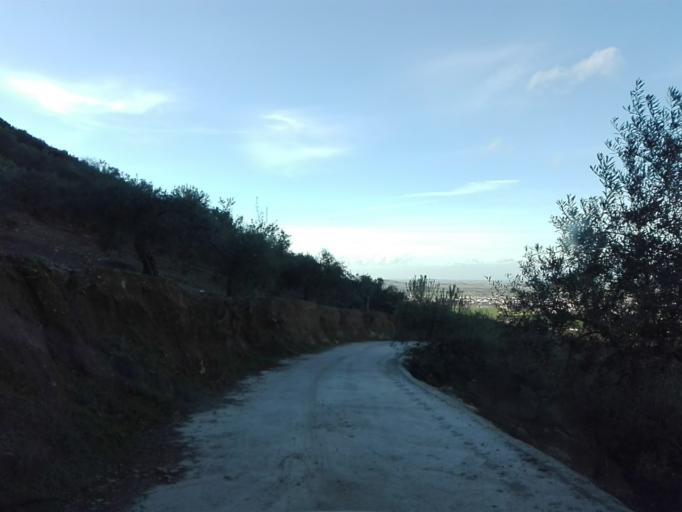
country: ES
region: Extremadura
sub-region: Provincia de Badajoz
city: Llerena
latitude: 38.2169
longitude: -6.0015
